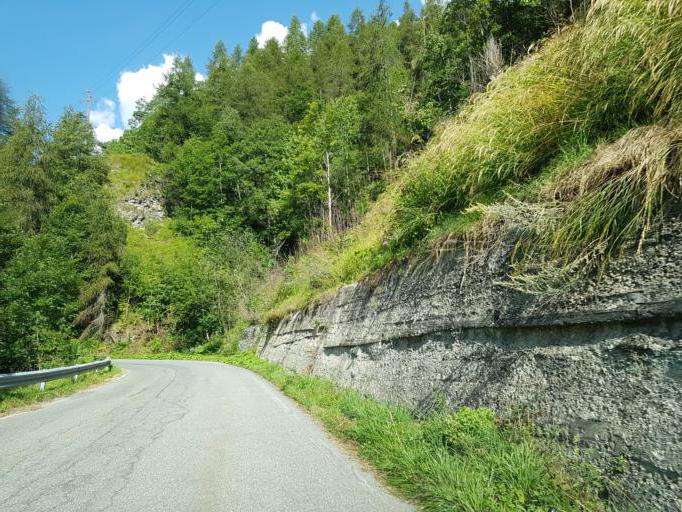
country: IT
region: Piedmont
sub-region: Provincia di Cuneo
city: Casteldelfino
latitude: 44.5864
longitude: 7.0599
